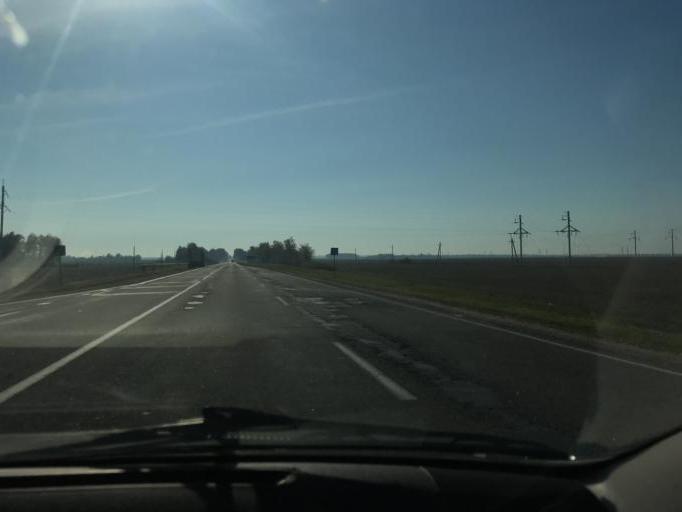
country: BY
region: Minsk
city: Salihorsk
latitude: 52.8500
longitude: 27.4665
